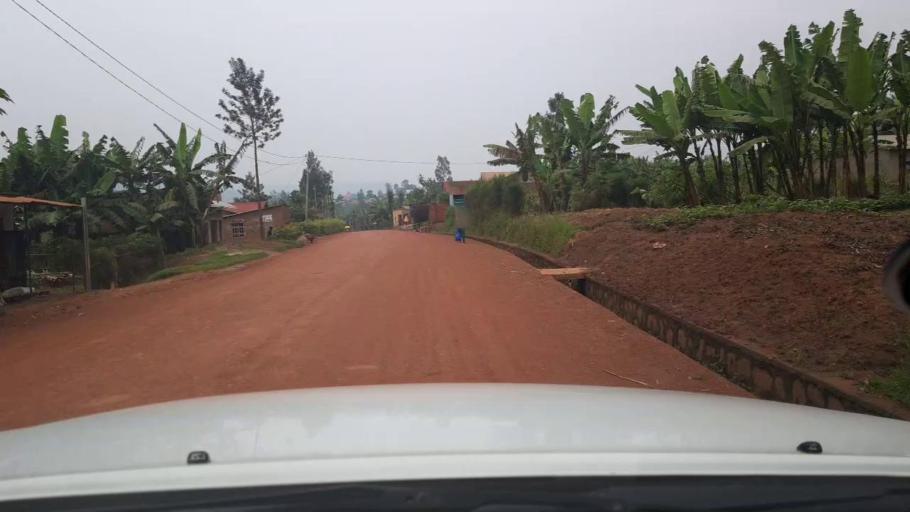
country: RW
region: Kigali
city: Kigali
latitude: -1.9024
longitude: 29.9717
